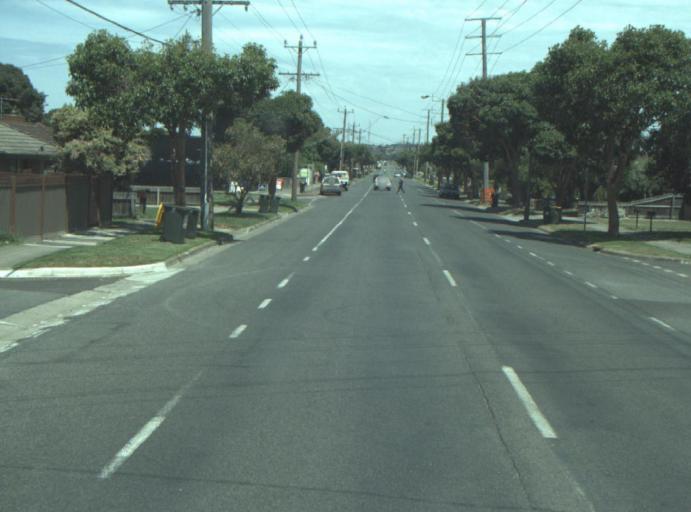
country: AU
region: Victoria
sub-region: Greater Geelong
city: Hamlyn Heights
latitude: -38.1300
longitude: 144.3199
